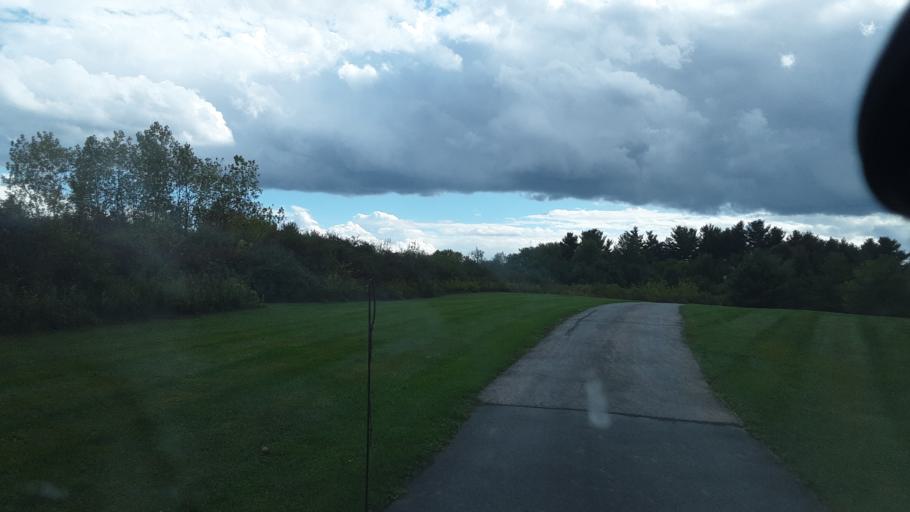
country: US
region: Ohio
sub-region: Knox County
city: Centerburg
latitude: 40.2997
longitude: -82.6869
